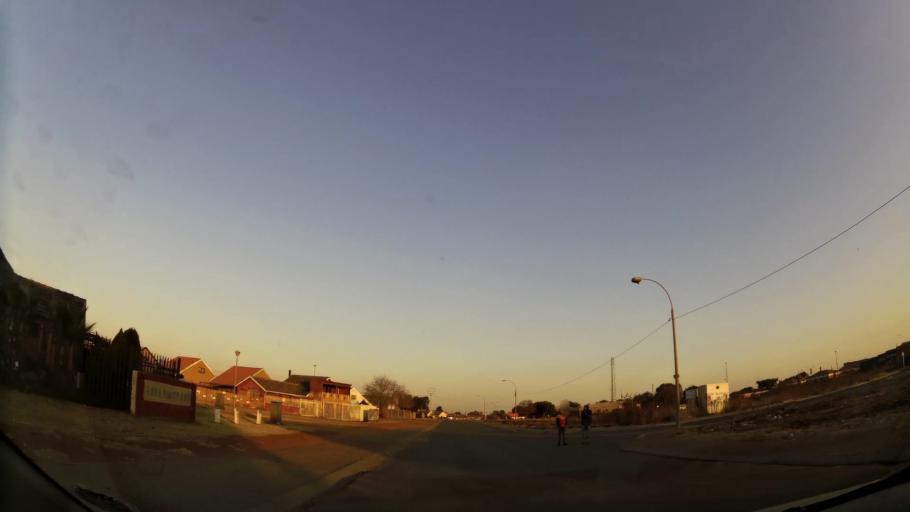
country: ZA
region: Gauteng
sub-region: West Rand District Municipality
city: Randfontein
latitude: -26.2024
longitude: 27.7066
